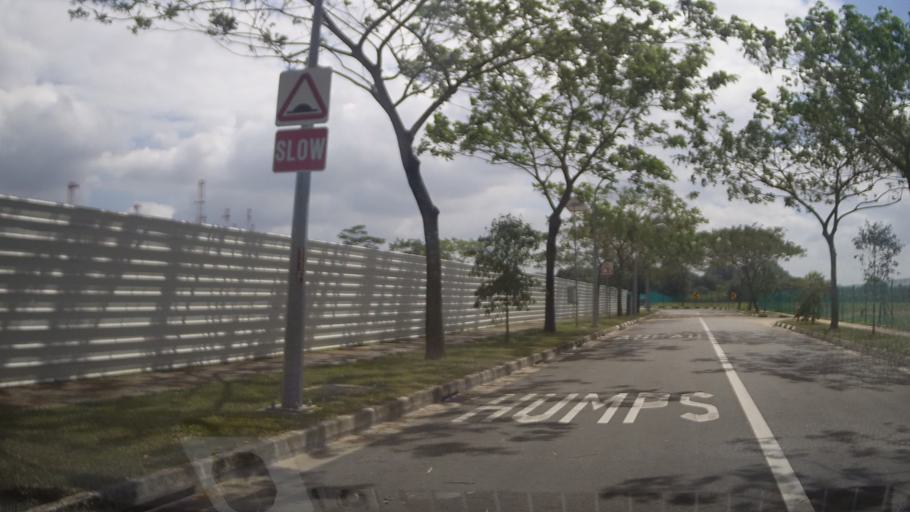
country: MY
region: Johor
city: Johor Bahru
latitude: 1.4205
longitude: 103.7243
